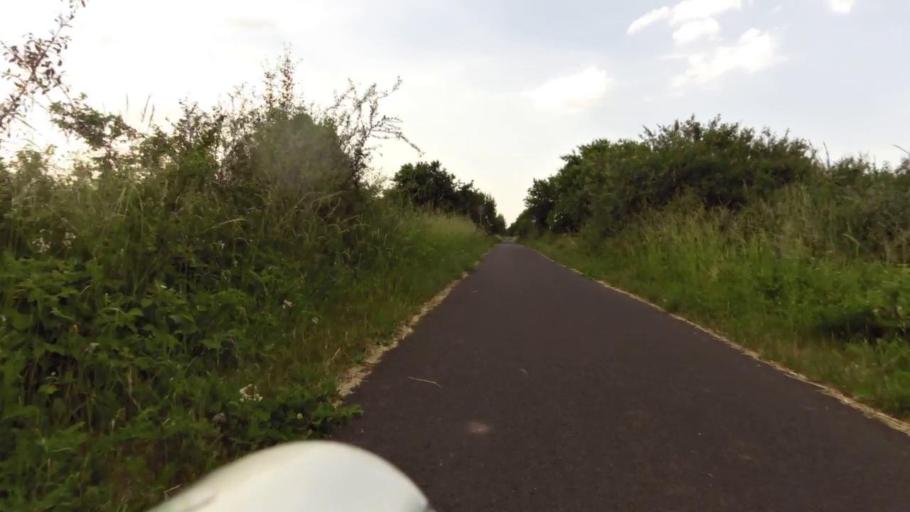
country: PL
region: Kujawsko-Pomorskie
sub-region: Powiat torunski
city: Lubianka
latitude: 53.1203
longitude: 18.4684
